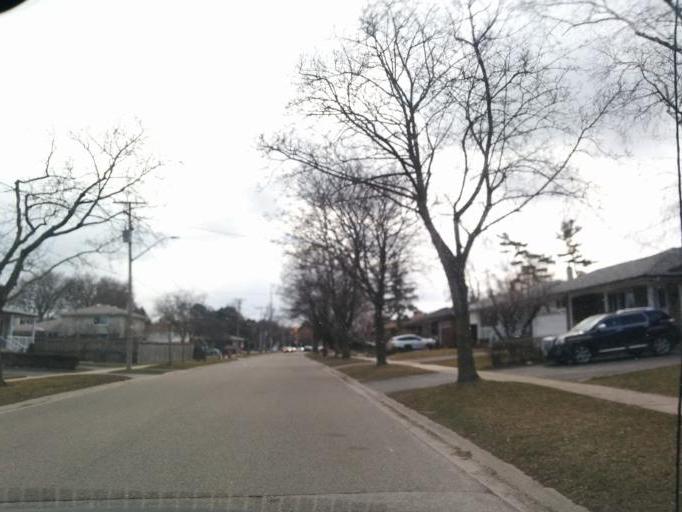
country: CA
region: Ontario
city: Etobicoke
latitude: 43.6010
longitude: -79.5690
